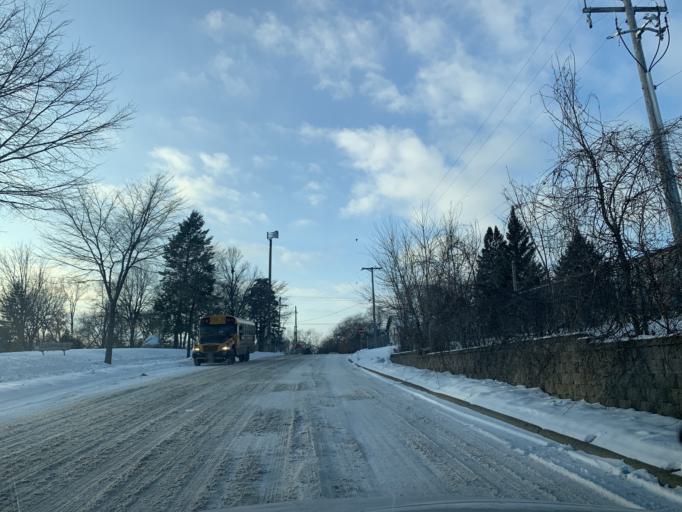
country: US
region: Minnesota
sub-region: Hennepin County
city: Minneapolis
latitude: 44.9881
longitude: -93.2972
